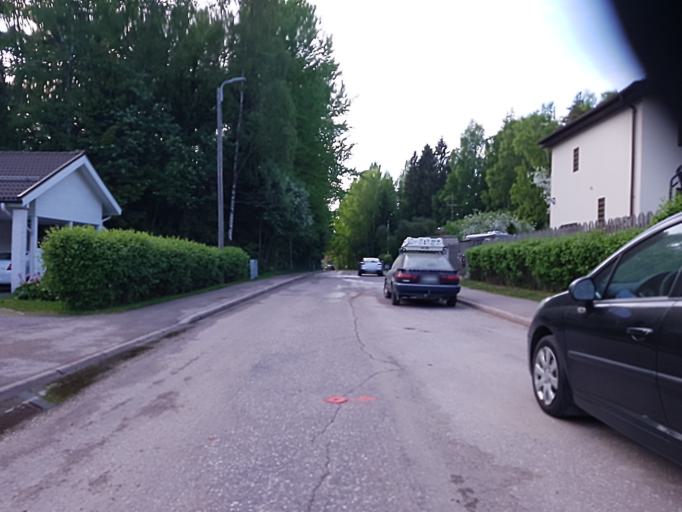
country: FI
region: Uusimaa
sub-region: Helsinki
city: Helsinki
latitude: 60.2509
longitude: 24.9346
